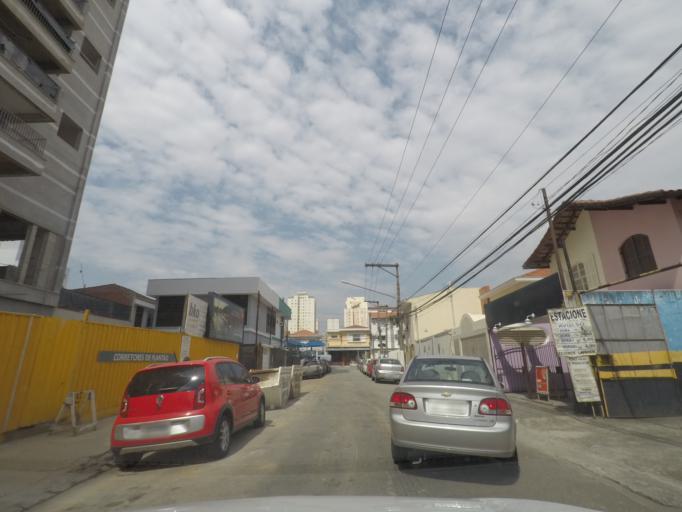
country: BR
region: Sao Paulo
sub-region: Sao Paulo
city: Sao Paulo
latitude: -23.6168
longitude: -46.6400
